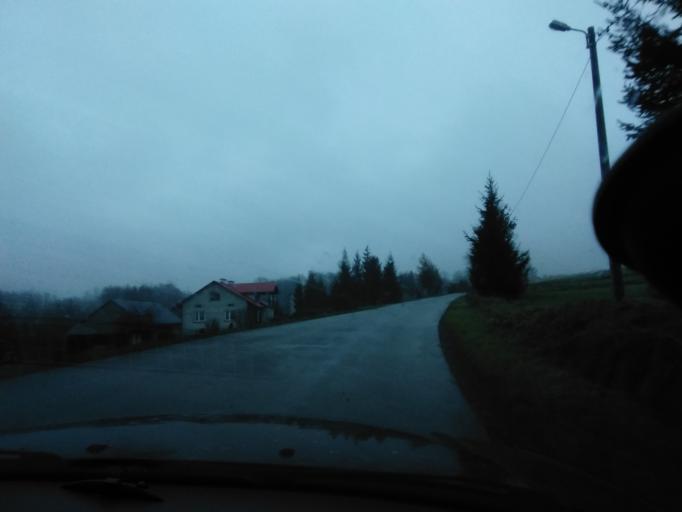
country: PL
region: Subcarpathian Voivodeship
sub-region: Powiat brzozowski
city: Jablonka
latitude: 49.7386
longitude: 22.1015
